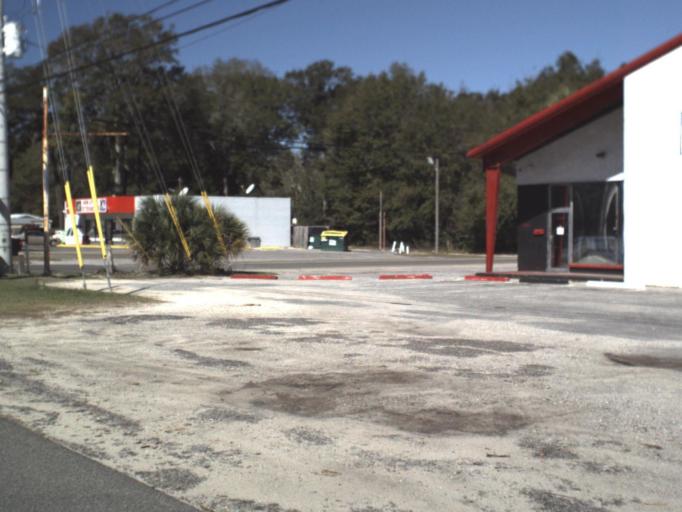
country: US
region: Florida
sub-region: Bay County
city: Springfield
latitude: 30.1531
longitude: -85.5991
